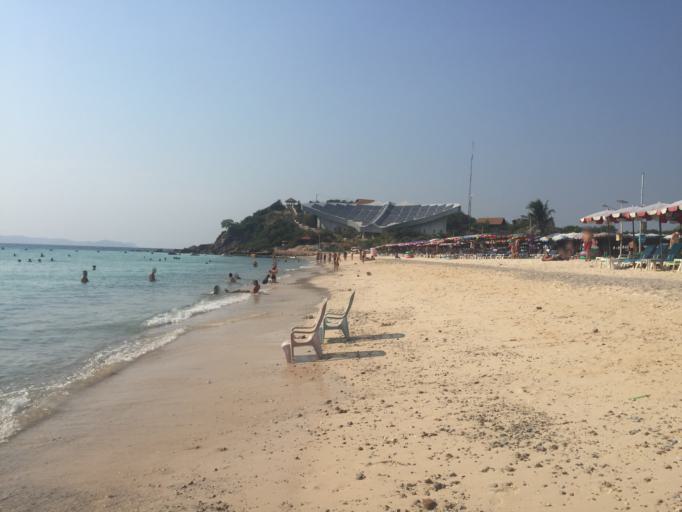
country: TH
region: Chon Buri
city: Ban Ko Lan
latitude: 12.9126
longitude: 100.7690
